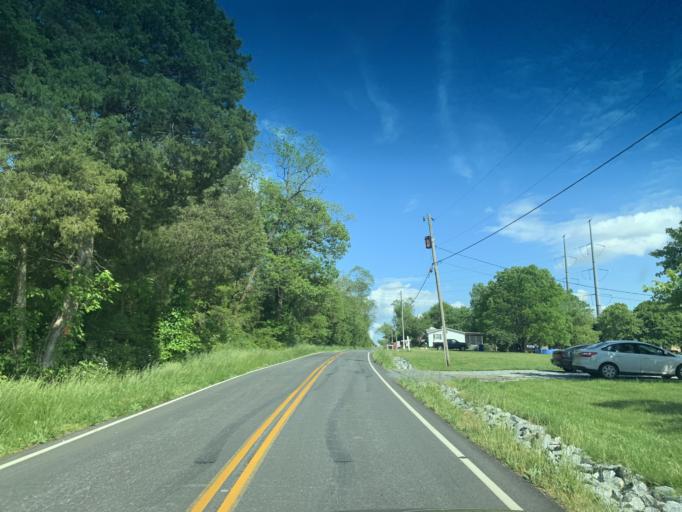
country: US
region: Maryland
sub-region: Cecil County
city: Rising Sun
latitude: 39.7180
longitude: -76.1650
